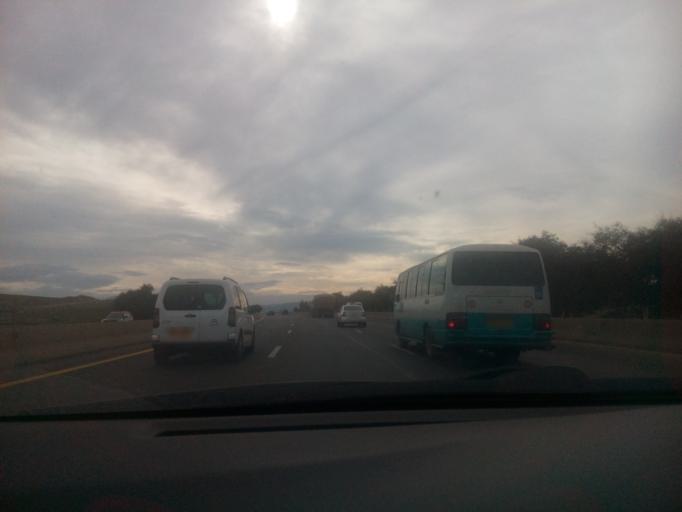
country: DZ
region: Oran
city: Es Senia
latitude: 35.5843
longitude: -0.5714
